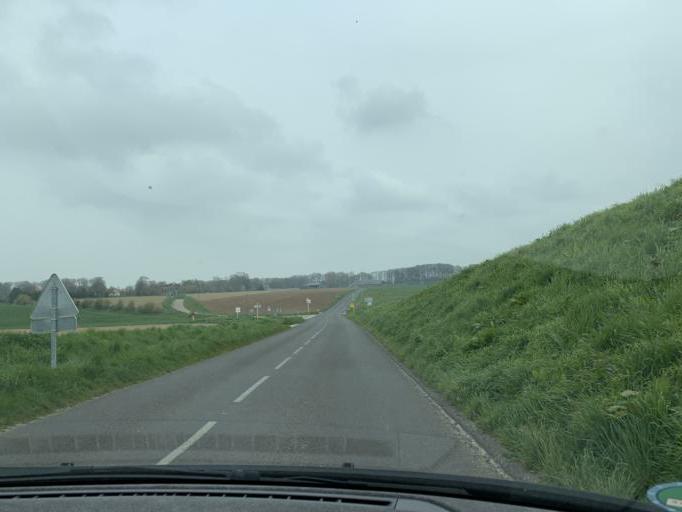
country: FR
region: Haute-Normandie
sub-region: Departement de la Seine-Maritime
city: Saint-Valery-en-Caux
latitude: 49.8537
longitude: 0.7809
